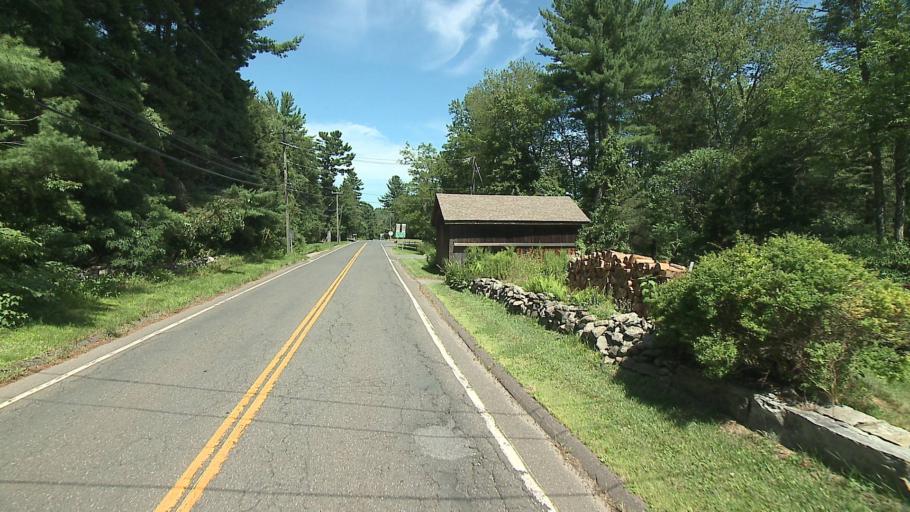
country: US
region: Connecticut
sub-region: Litchfield County
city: New Hartford Center
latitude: 41.9141
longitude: -72.9780
